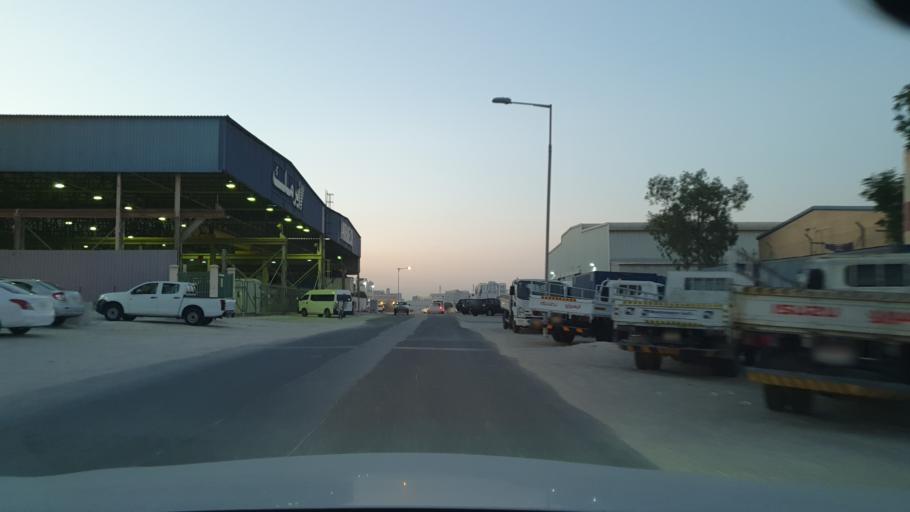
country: BH
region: Northern
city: Ar Rifa'
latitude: 26.1252
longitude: 50.5878
